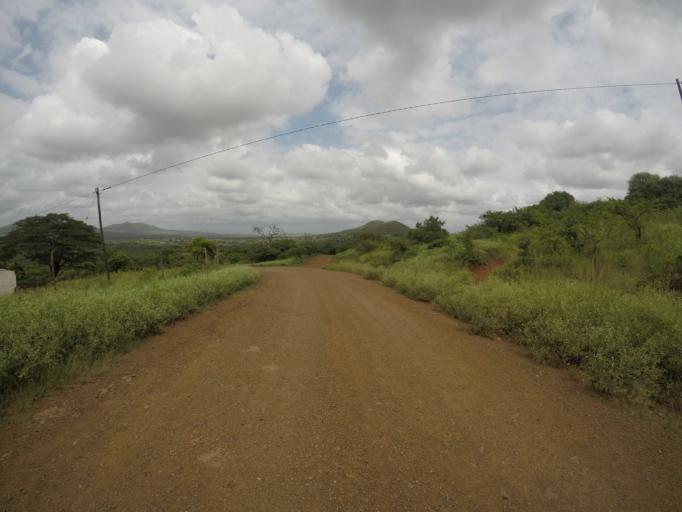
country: ZA
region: KwaZulu-Natal
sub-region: uThungulu District Municipality
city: Empangeni
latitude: -28.5948
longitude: 31.8793
